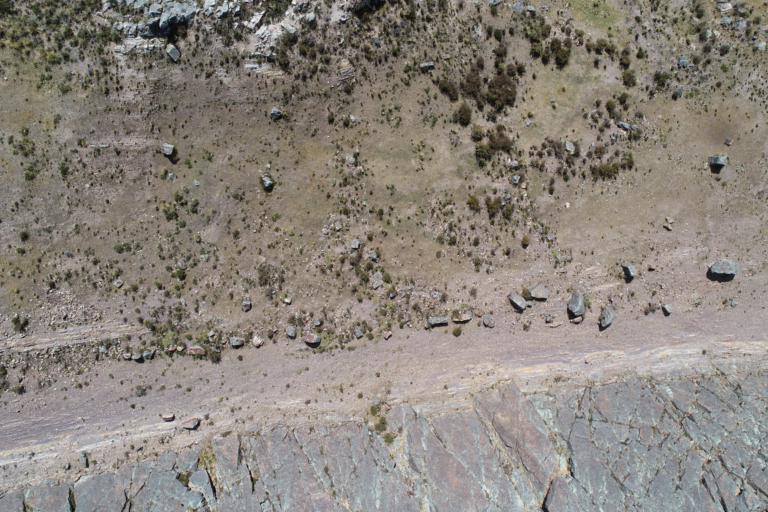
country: BO
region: La Paz
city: Achacachi
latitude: -15.8945
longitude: -68.9045
